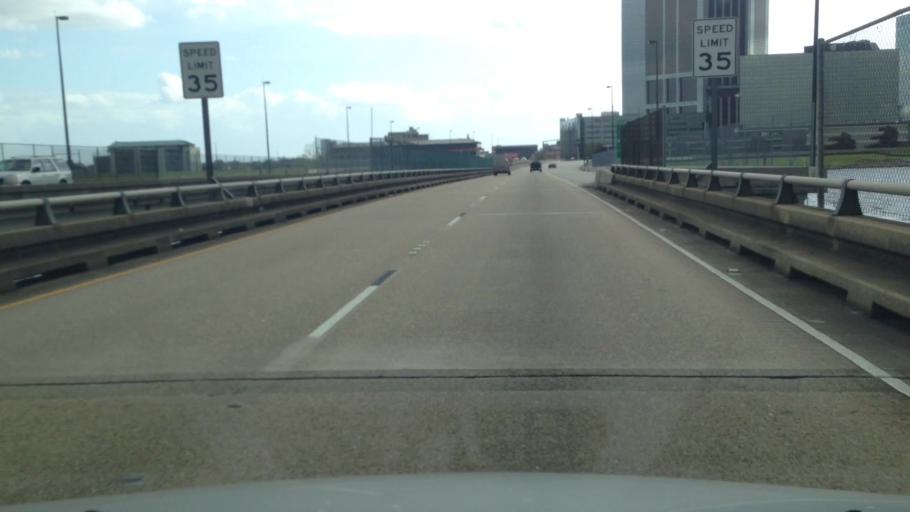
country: US
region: Louisiana
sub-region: Jefferson Parish
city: Metairie
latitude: 30.0234
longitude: -90.1538
